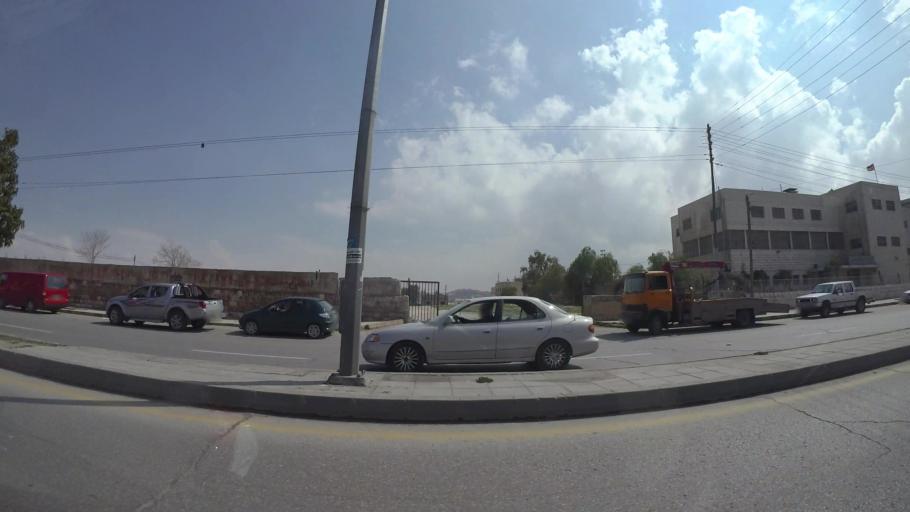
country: JO
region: Zarqa
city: Russeifa
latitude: 31.9861
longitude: 35.9978
